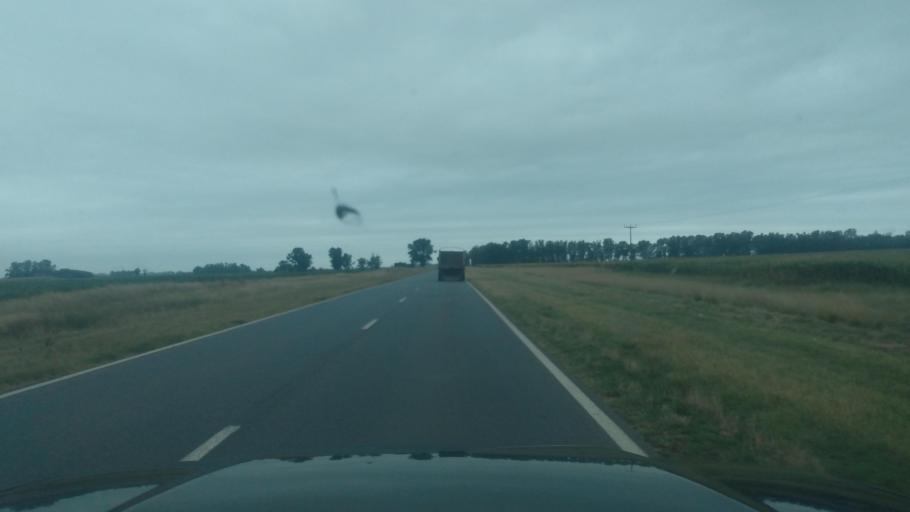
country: AR
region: Buenos Aires
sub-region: Partido de Nueve de Julio
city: Nueve de Julio
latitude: -35.4086
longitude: -60.7741
